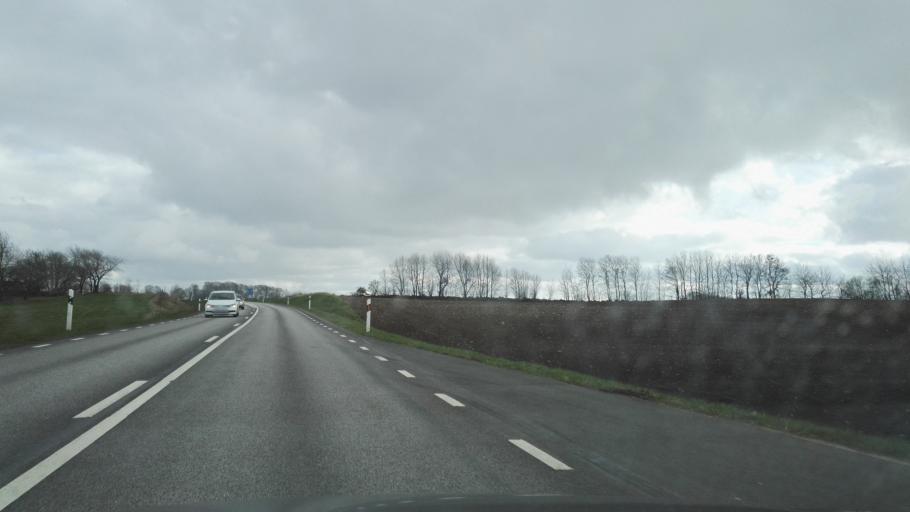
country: SE
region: Skane
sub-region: Horby Kommun
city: Hoerby
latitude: 55.7623
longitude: 13.6760
